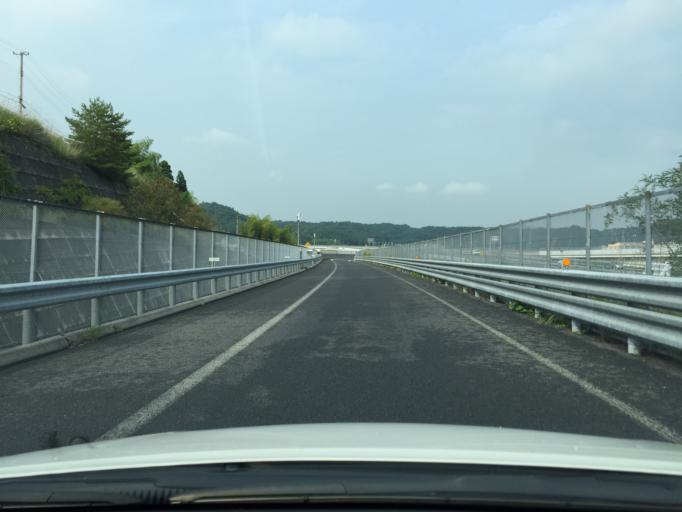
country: JP
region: Fukushima
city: Iwaki
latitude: 37.0656
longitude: 140.8355
